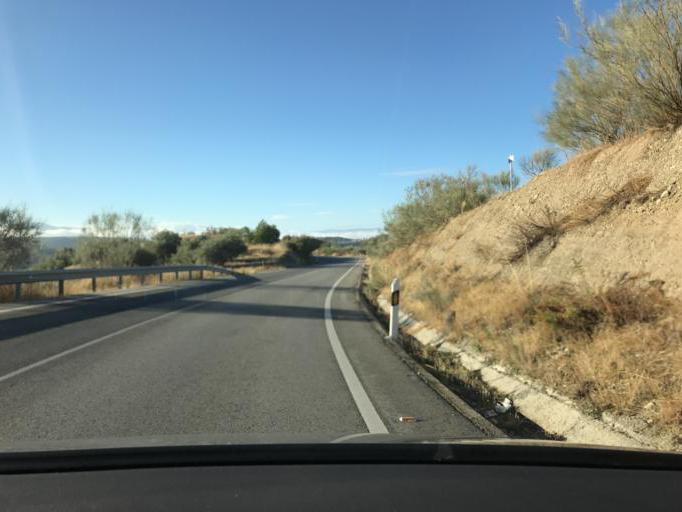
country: ES
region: Andalusia
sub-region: Provincia de Granada
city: Viznar
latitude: 37.2187
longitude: -3.5635
